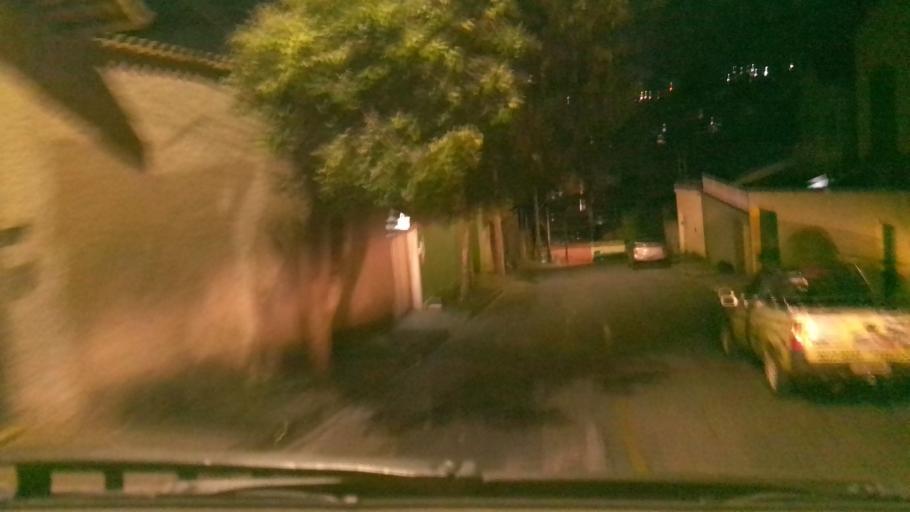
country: BR
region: Minas Gerais
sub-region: Belo Horizonte
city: Belo Horizonte
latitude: -19.9103
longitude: -43.9003
